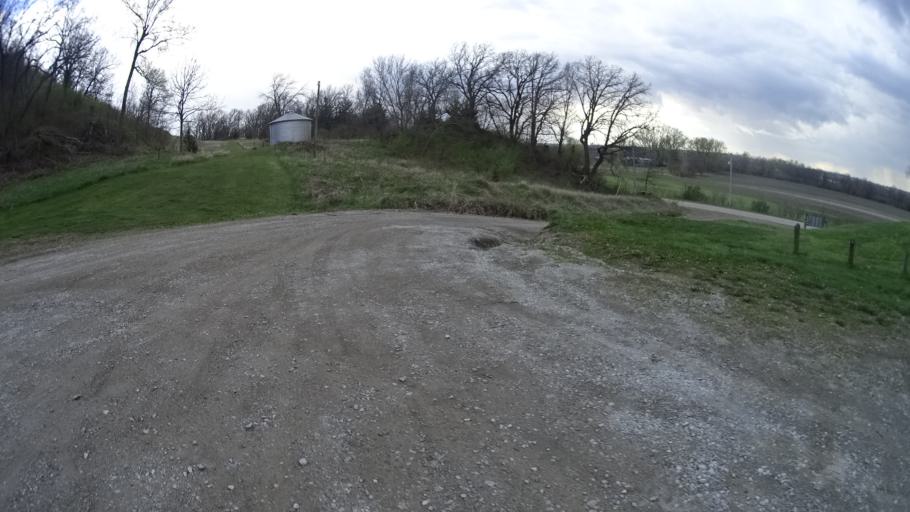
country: US
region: Iowa
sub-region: Mills County
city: Glenwood
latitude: 41.0754
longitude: -95.8120
